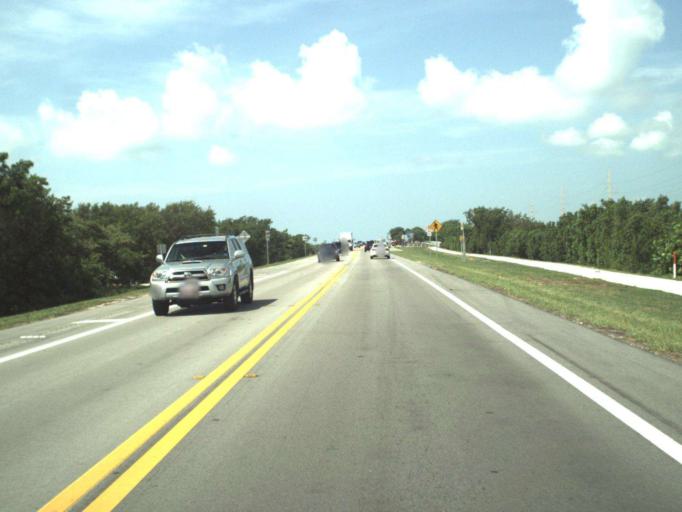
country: US
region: Florida
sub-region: Monroe County
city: Islamorada
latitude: 24.8473
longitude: -80.7439
